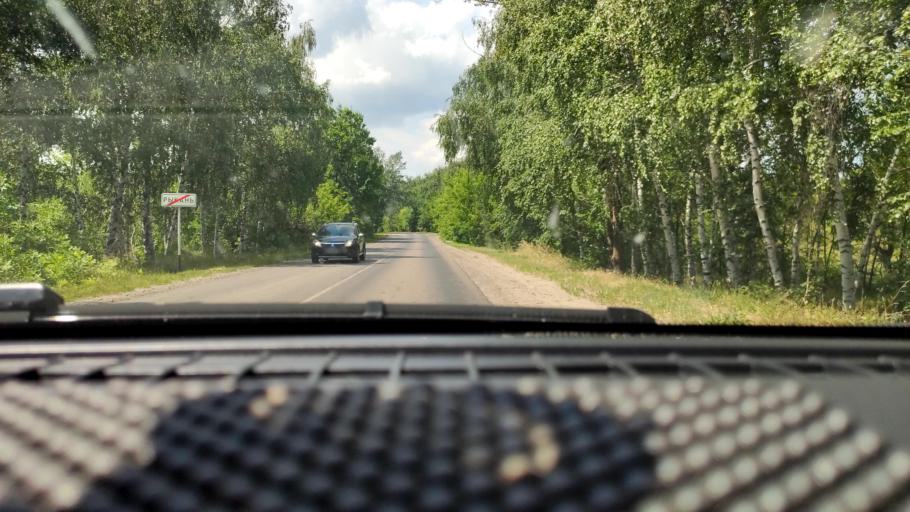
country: RU
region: Voronezj
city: Podkletnoye
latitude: 51.6231
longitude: 39.5565
